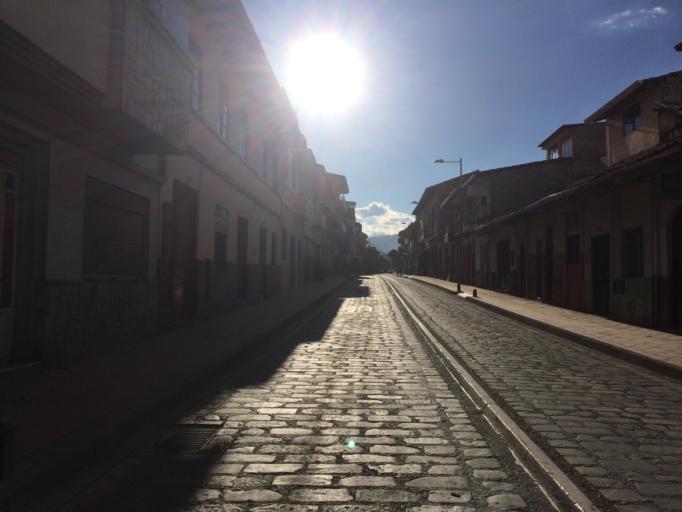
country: EC
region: Azuay
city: Cuenca
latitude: -2.8925
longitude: -79.0093
